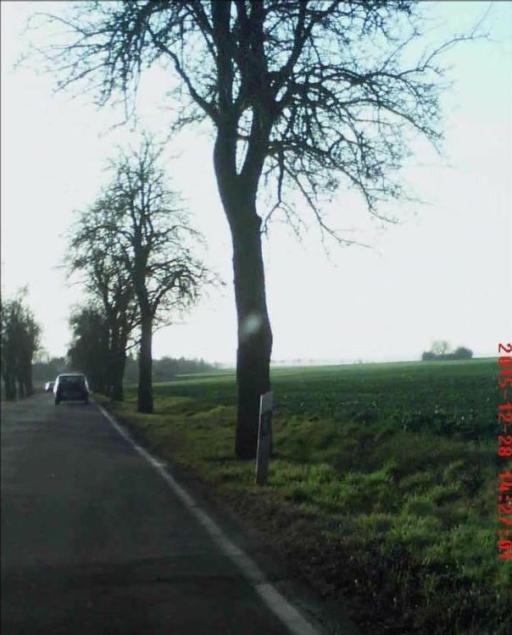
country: DE
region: Thuringia
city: Goldbach
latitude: 51.0526
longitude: 11.4178
